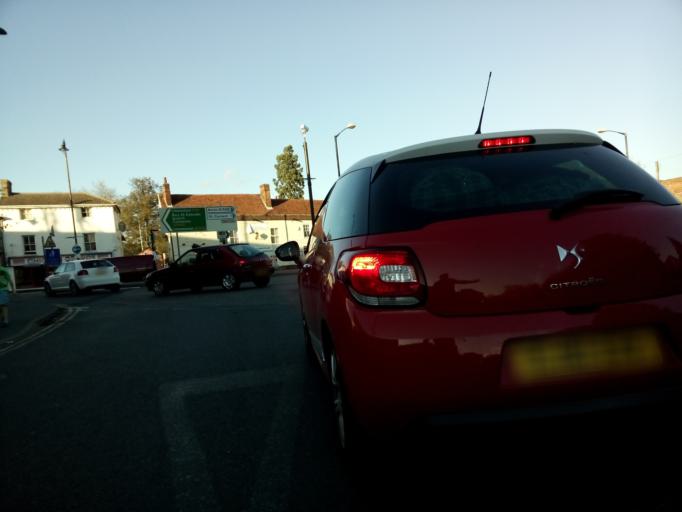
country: GB
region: England
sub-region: Suffolk
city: Sudbury
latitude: 52.0380
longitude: 0.7330
